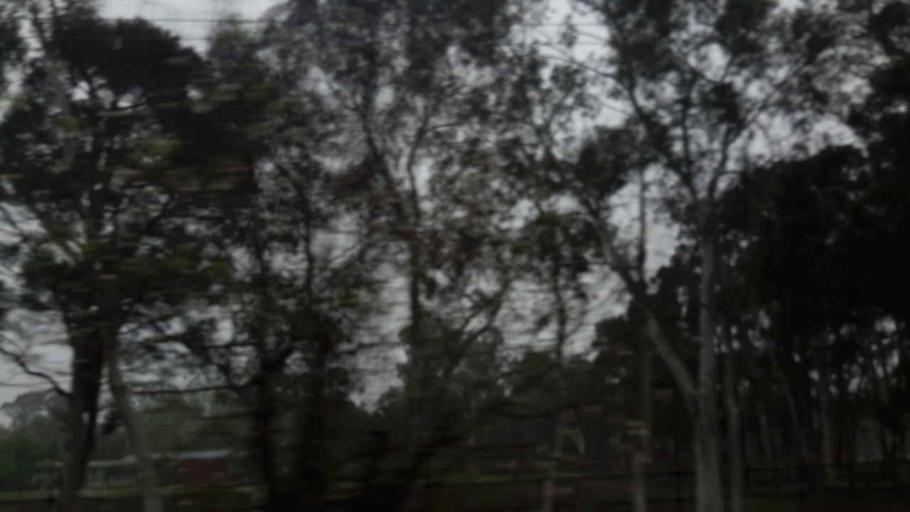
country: AU
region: New South Wales
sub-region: Penrith Municipality
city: Werrington Downs
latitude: -33.6870
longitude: 150.7328
